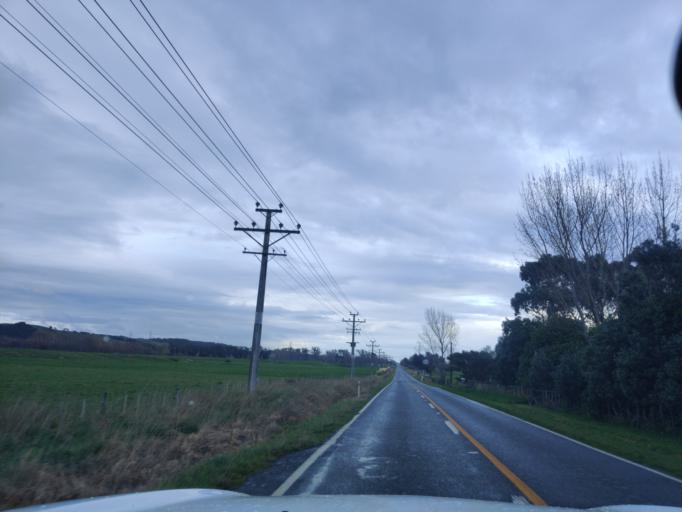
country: NZ
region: Manawatu-Wanganui
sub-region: Palmerston North City
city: Palmerston North
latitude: -40.3391
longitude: 175.7210
